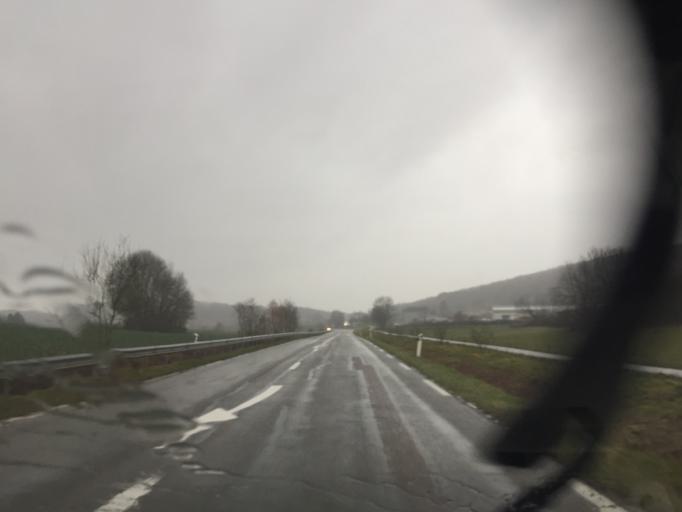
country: FR
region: Franche-Comte
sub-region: Departement du Jura
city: Mouchard
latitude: 46.9848
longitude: 5.8185
